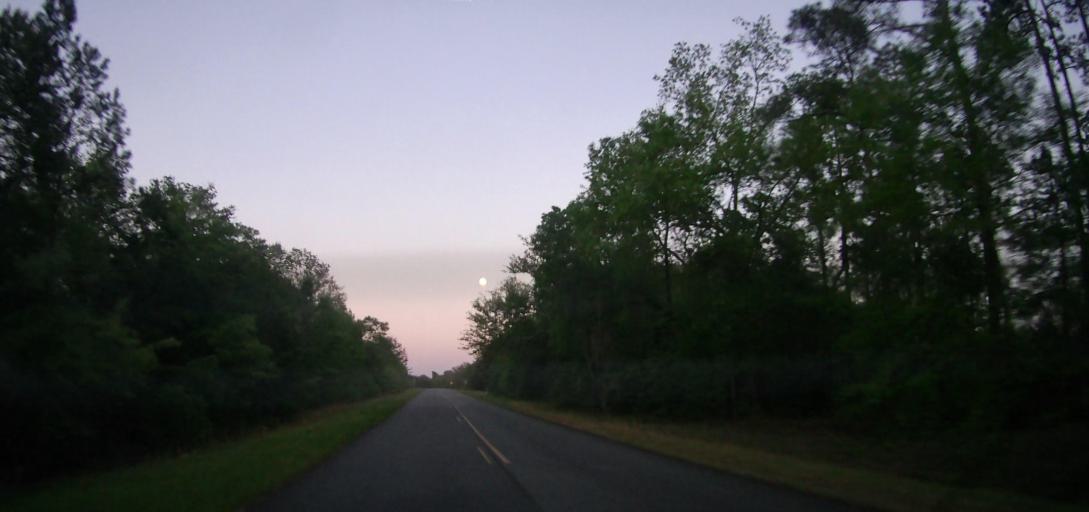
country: US
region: Georgia
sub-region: Marion County
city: Buena Vista
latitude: 32.2541
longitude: -84.6151
